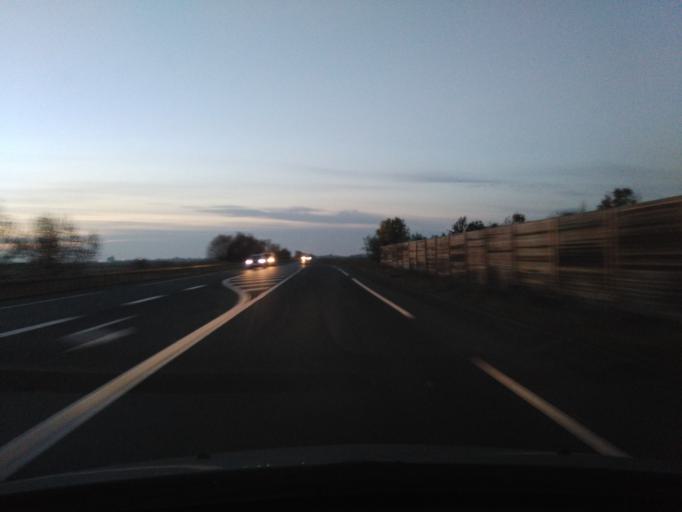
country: FR
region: Pays de la Loire
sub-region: Departement de la Vendee
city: Champagne-les-Marais
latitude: 46.3999
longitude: -1.0962
